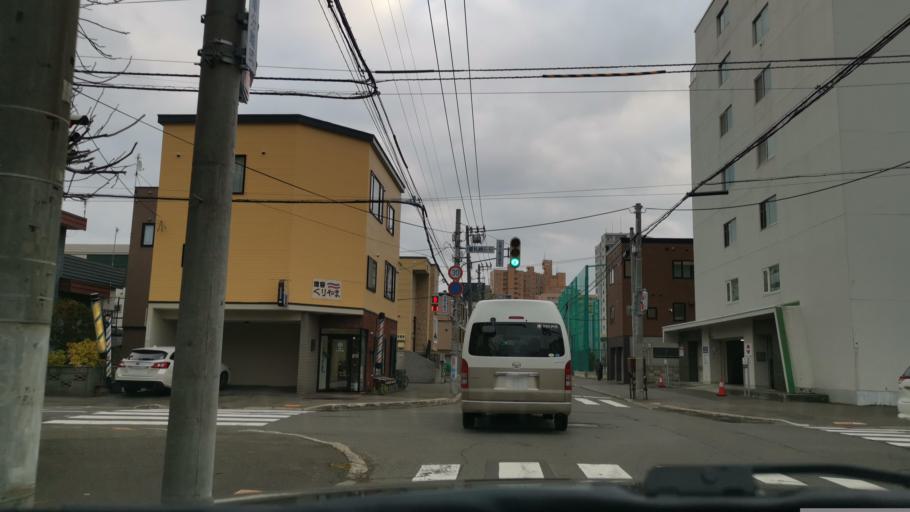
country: JP
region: Hokkaido
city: Sapporo
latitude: 43.0491
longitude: 141.3947
